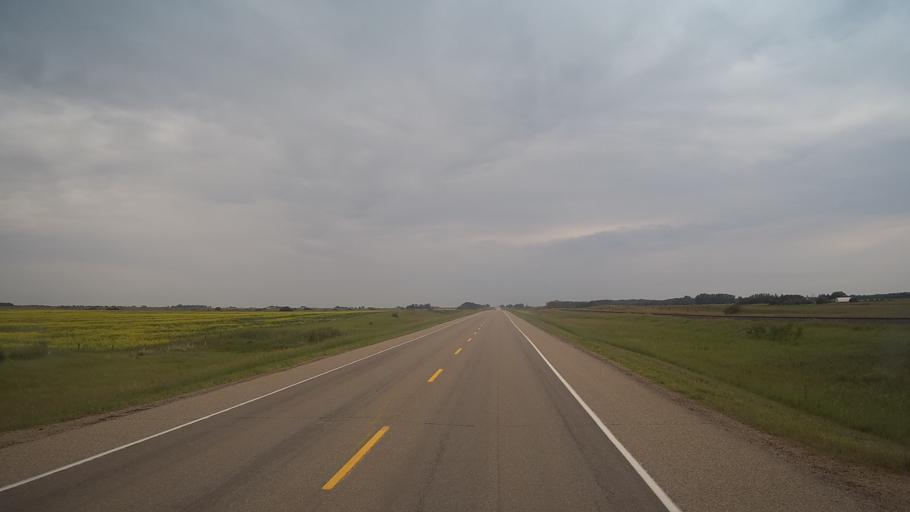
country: CA
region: Saskatchewan
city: Langham
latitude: 52.1275
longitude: -107.2533
